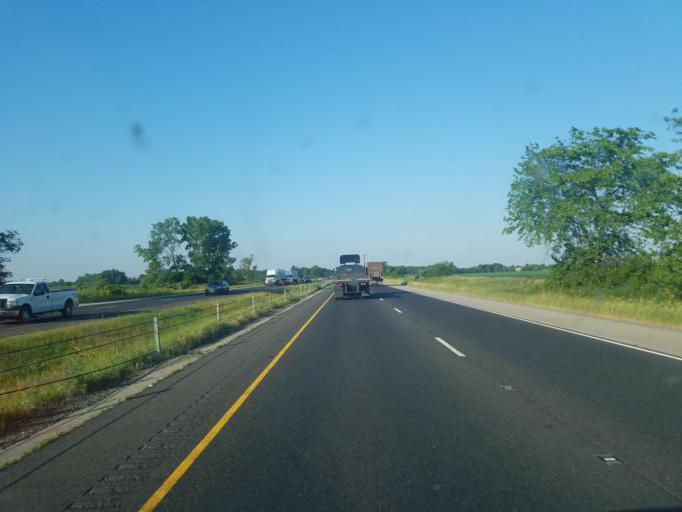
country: US
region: Illinois
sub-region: Grundy County
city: Minooka
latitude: 41.4807
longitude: -88.2310
